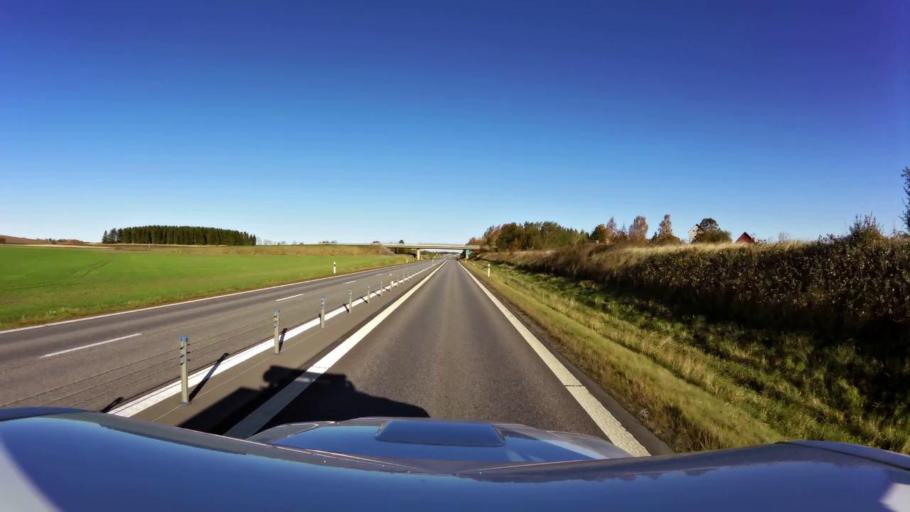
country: SE
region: OEstergoetland
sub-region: Linkopings Kommun
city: Berg
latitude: 58.4667
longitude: 15.4943
